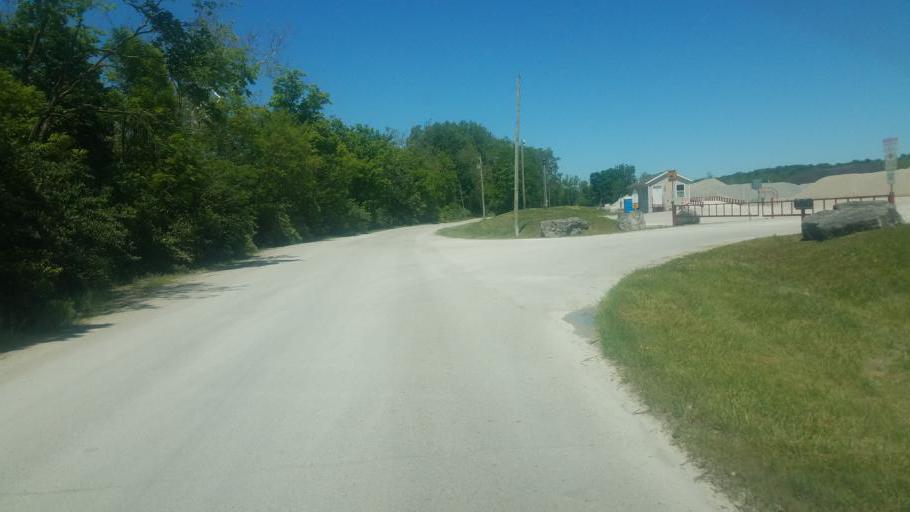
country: US
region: Ohio
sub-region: Miami County
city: Piqua
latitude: 40.2178
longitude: -84.2118
